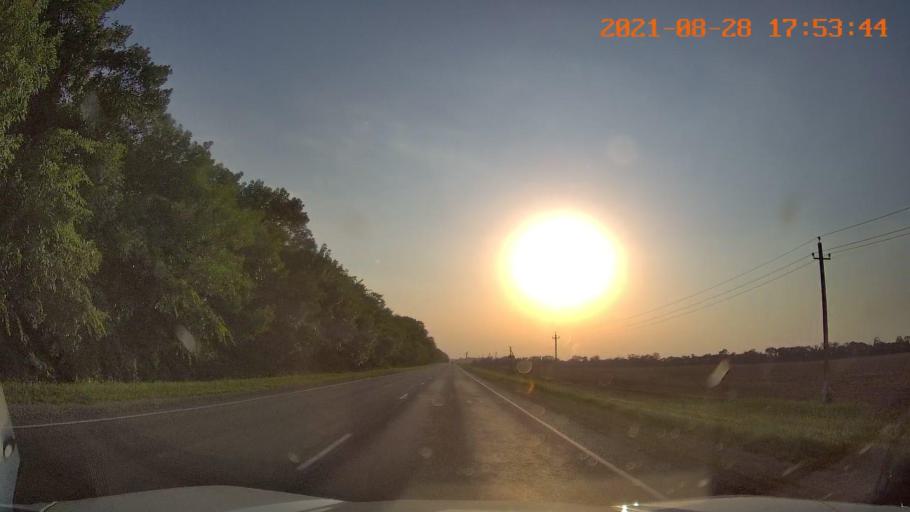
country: RU
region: Krasnodarskiy
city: Konstantinovskaya
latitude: 44.9375
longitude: 40.7524
